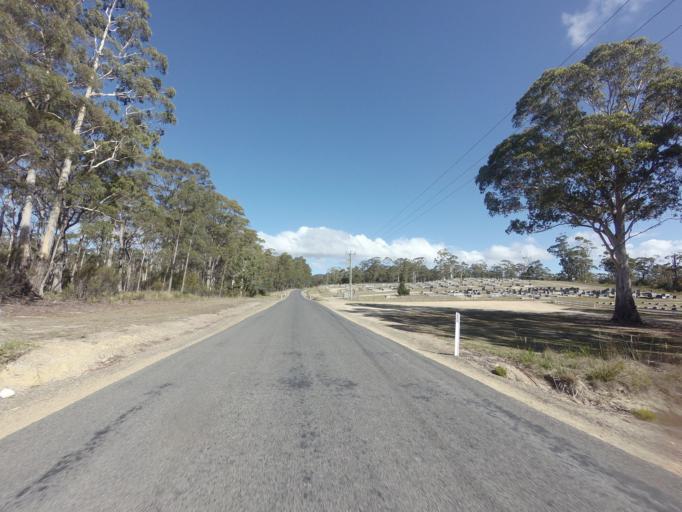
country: AU
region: Tasmania
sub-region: Break O'Day
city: St Helens
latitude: -41.5979
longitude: 148.2041
